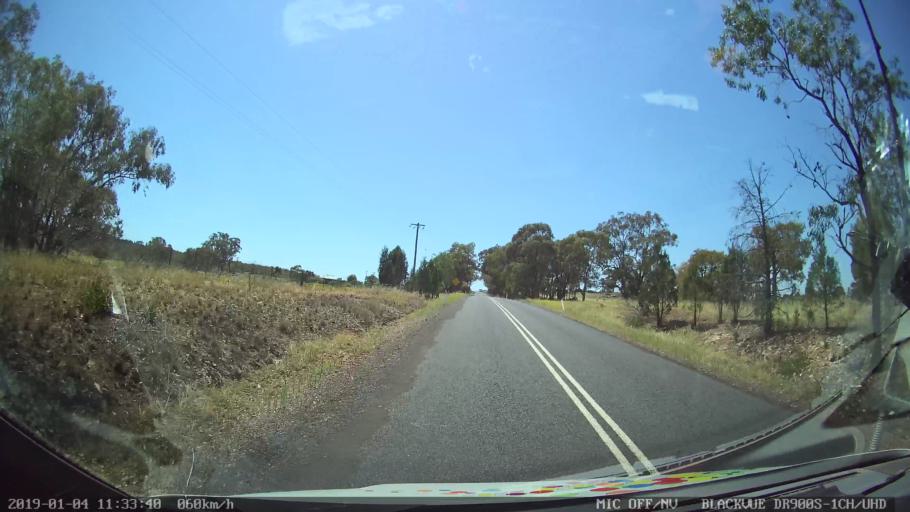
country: AU
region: New South Wales
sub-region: Cabonne
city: Molong
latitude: -33.0659
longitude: 148.8202
